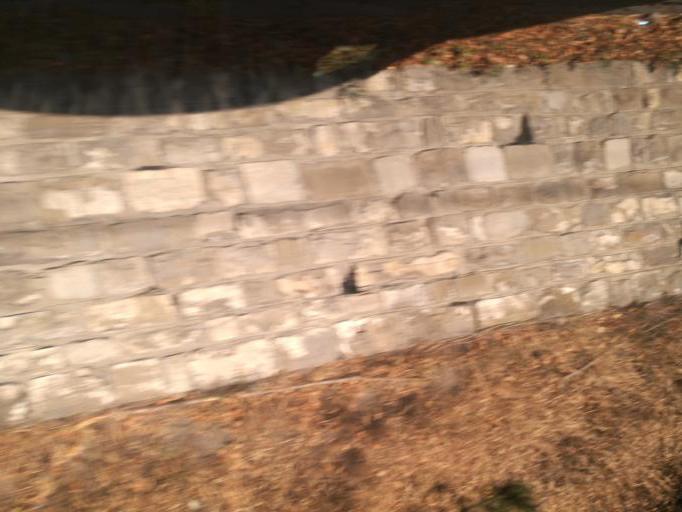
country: RO
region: Prahova
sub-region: Comuna Comarnic
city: Posada
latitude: 45.2907
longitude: 25.6118
